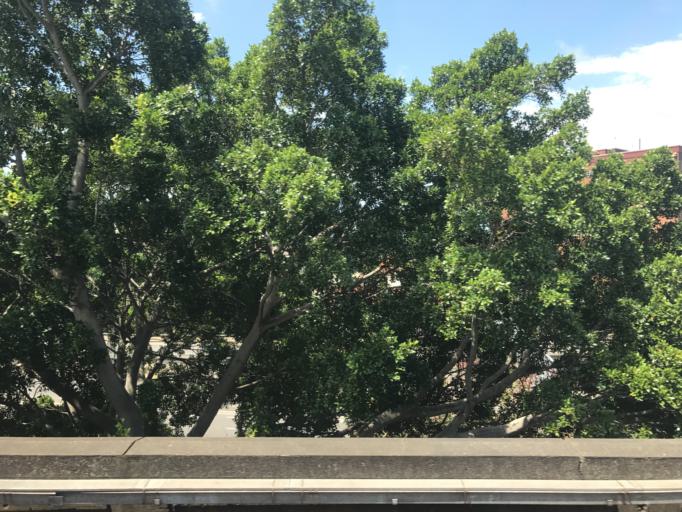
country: AU
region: New South Wales
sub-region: North Sydney
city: Milsons Point
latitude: -33.8435
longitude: 151.2108
